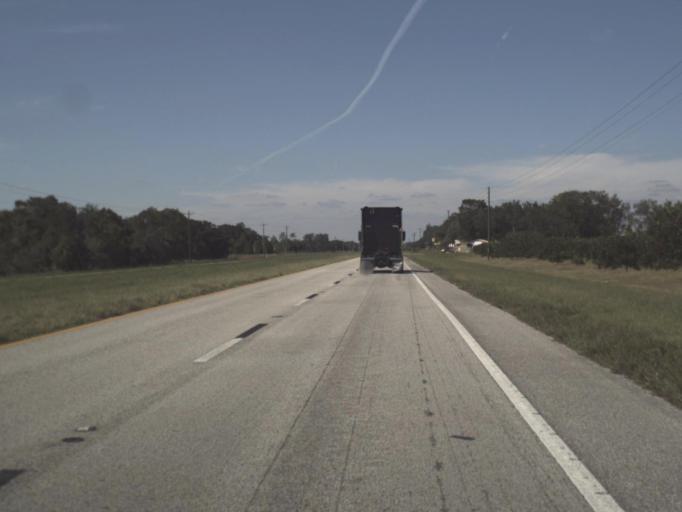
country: US
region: Florida
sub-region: Highlands County
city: Lake Placid
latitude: 27.3819
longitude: -81.4075
